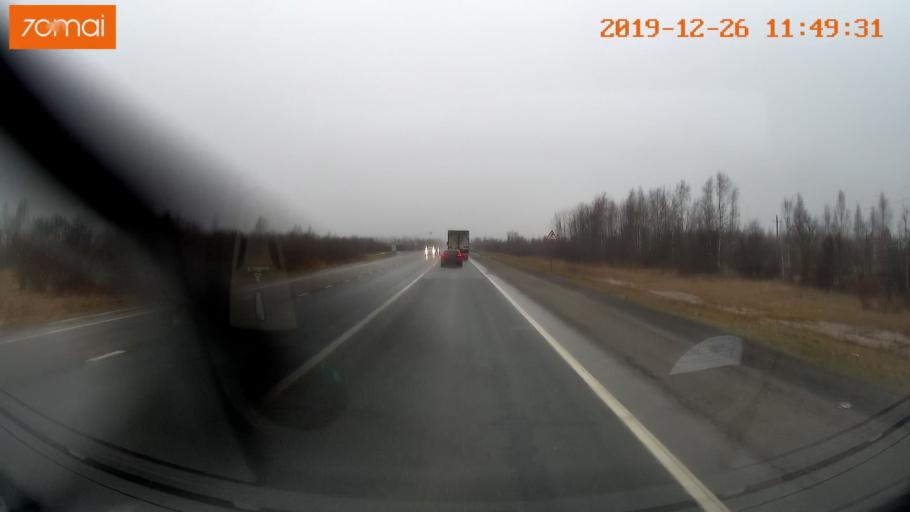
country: RU
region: Vologda
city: Sheksna
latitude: 59.2489
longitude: 38.4186
